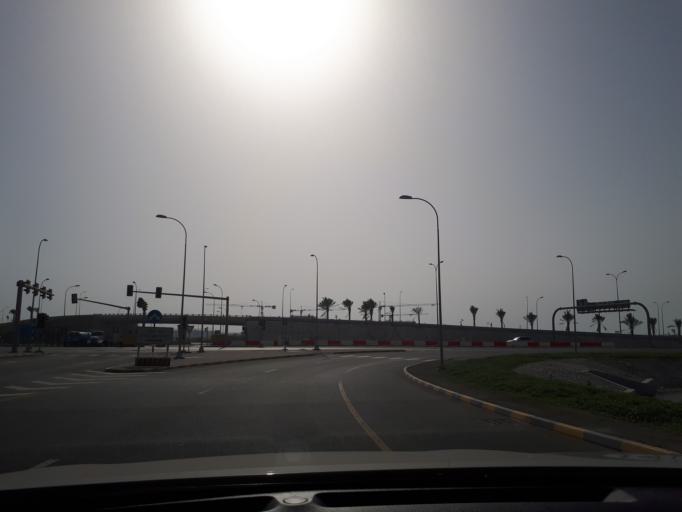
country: OM
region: Muhafazat Masqat
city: Bawshar
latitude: 23.6046
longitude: 58.3121
